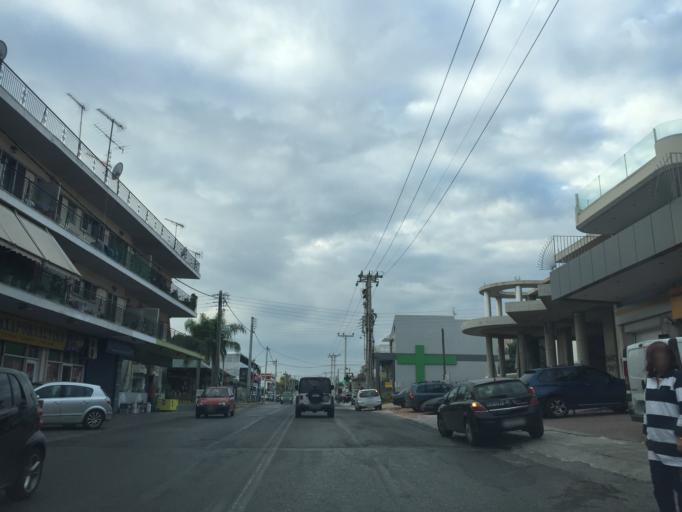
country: GR
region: Attica
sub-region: Nomarchia Anatolikis Attikis
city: Vari
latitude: 37.8335
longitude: 23.8018
